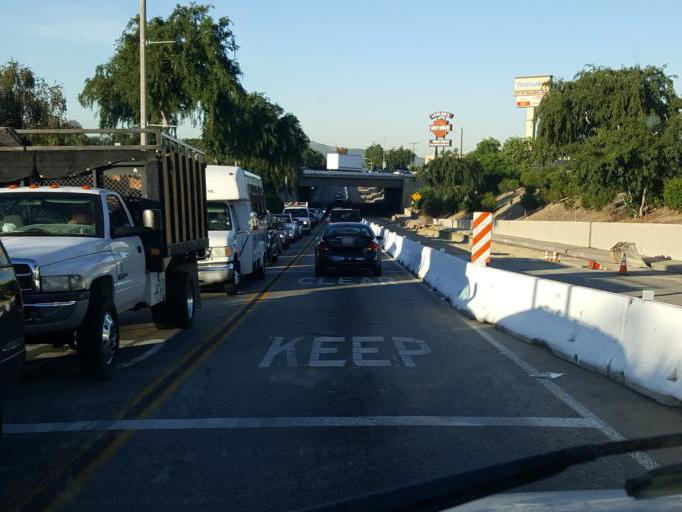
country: US
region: California
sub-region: Los Angeles County
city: Baldwin Park
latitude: 34.0715
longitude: -117.9607
